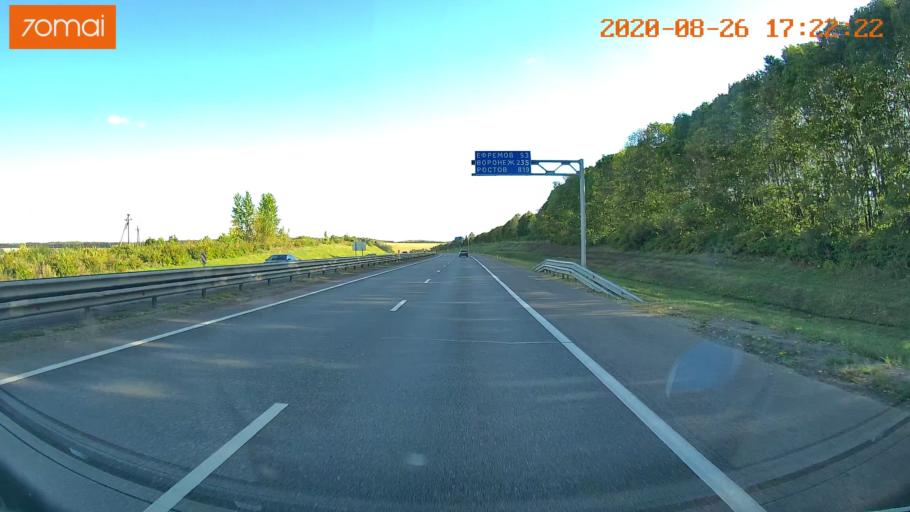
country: RU
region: Tula
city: Volovo
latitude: 53.5510
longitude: 38.1125
